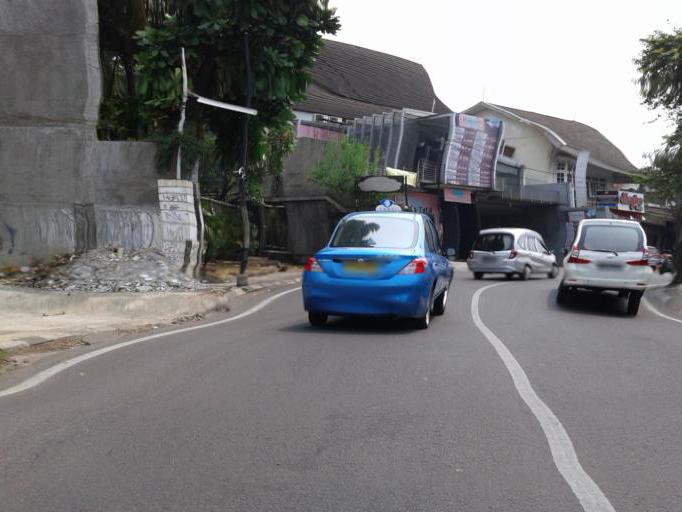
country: ID
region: Banten
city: South Tangerang
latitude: -6.2721
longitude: 106.7553
